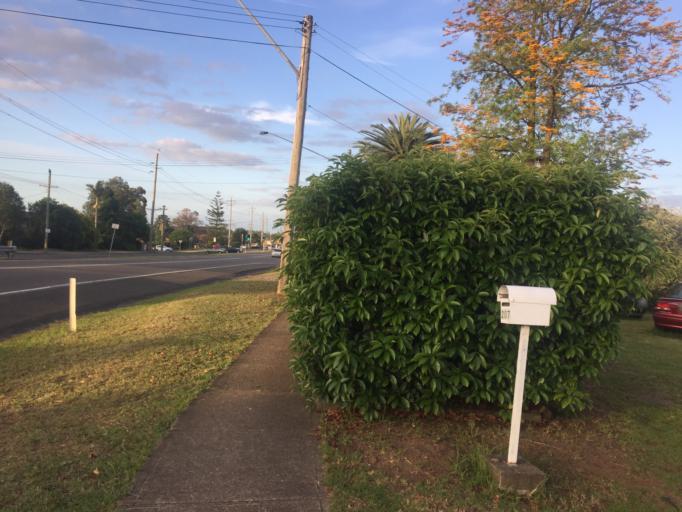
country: AU
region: New South Wales
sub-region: Blacktown
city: Blacktown
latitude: -33.7890
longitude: 150.9194
